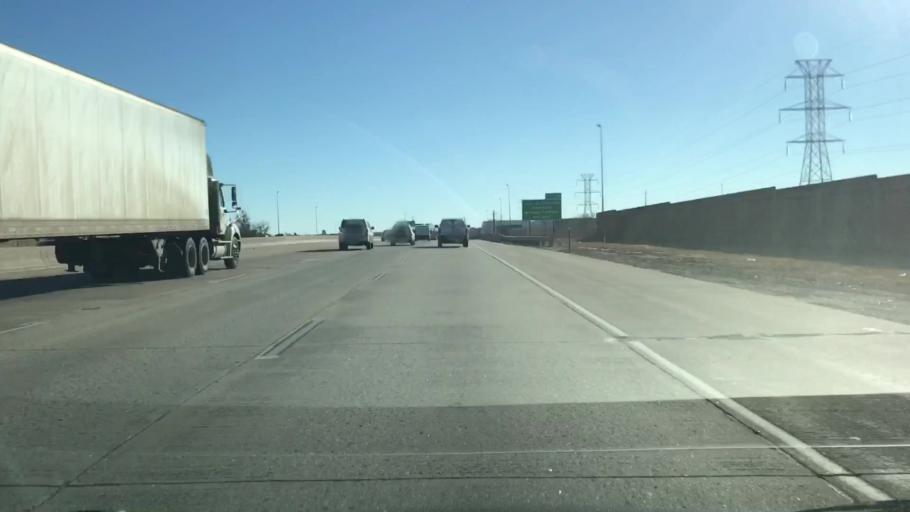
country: US
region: Colorado
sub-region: Adams County
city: Aurora
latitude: 39.7582
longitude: -104.8279
